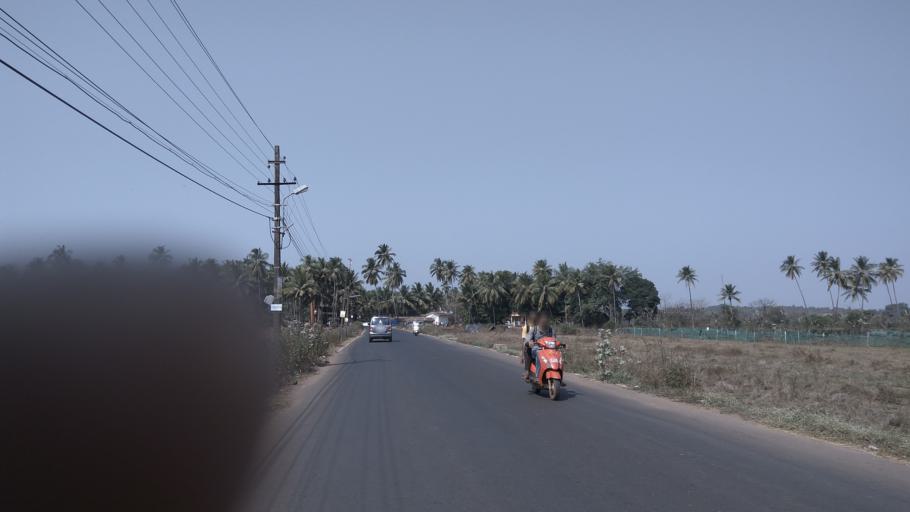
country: IN
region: Goa
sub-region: North Goa
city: Vagator
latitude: 15.5930
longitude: 73.7591
